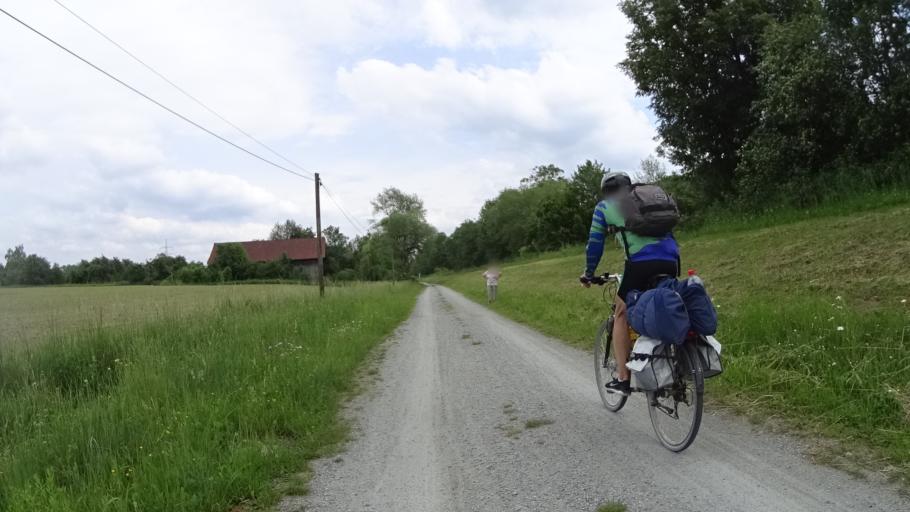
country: DE
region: Bavaria
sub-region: Lower Bavaria
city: Aicha vorm Wald
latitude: 48.6054
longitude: 13.3149
